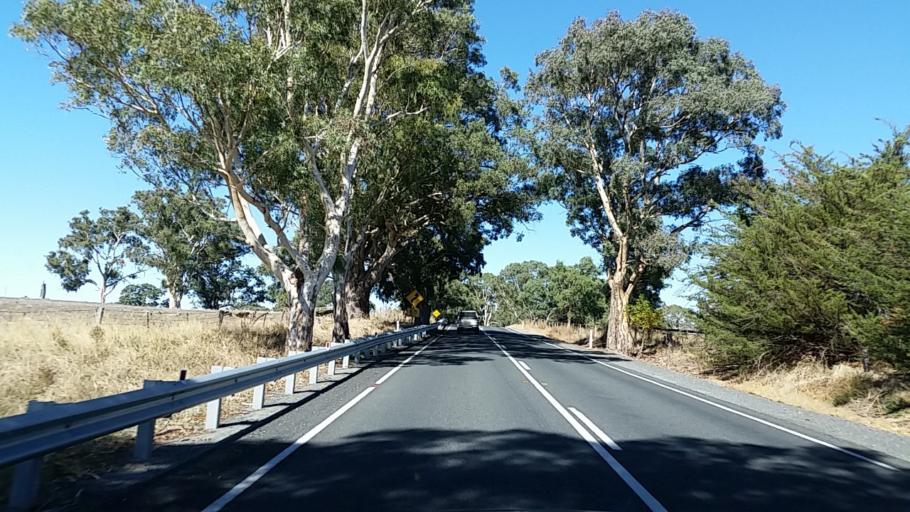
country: AU
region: South Australia
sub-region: Adelaide Hills
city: Birdwood
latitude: -34.7756
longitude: 139.0313
